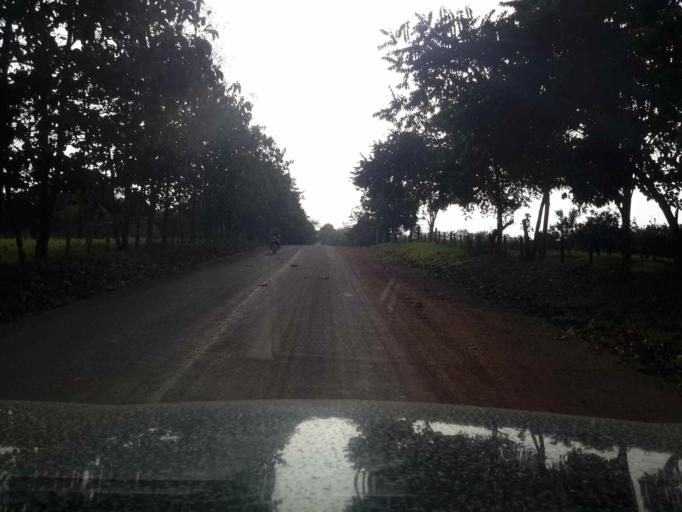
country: CR
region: Alajuela
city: Los Chiles
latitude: 11.1489
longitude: -84.6431
